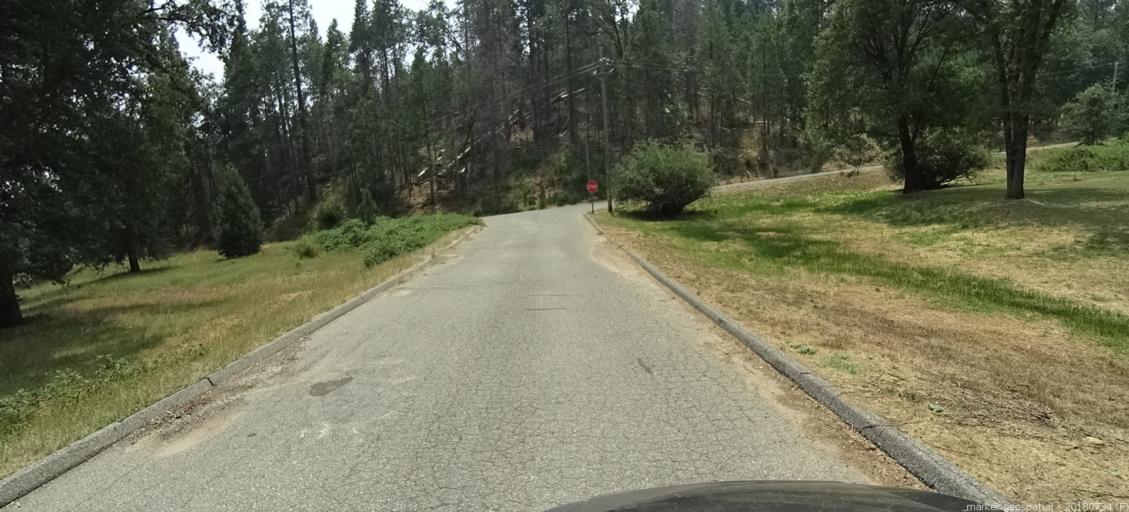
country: US
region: California
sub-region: Madera County
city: Oakhurst
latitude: 37.2728
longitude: -119.5800
